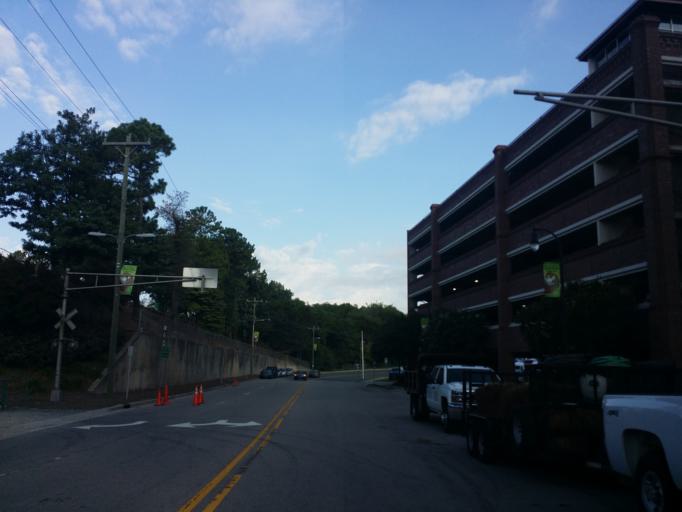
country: US
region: North Carolina
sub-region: Durham County
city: Durham
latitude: 35.9915
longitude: -78.9060
